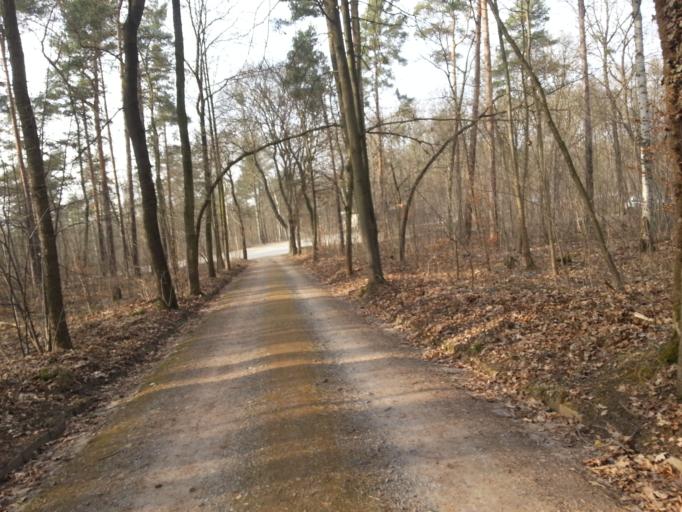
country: DE
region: Saxony
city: Albertstadt
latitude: 51.0809
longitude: 13.7764
